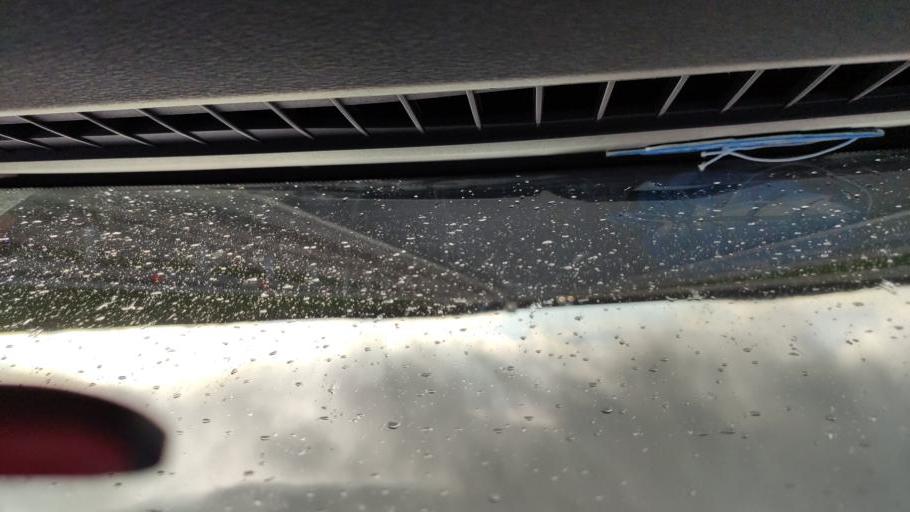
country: RU
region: Saratov
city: Yelshanka
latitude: 51.8322
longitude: 46.4613
